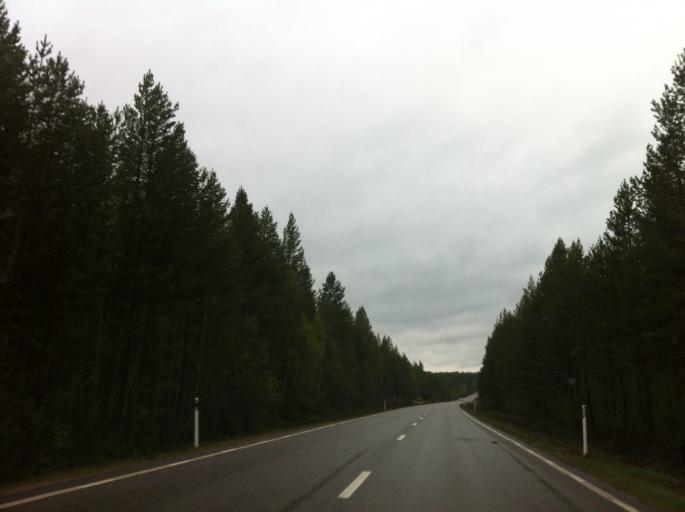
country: SE
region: Jaemtland
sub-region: Harjedalens Kommun
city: Sveg
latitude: 62.1079
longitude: 14.1946
